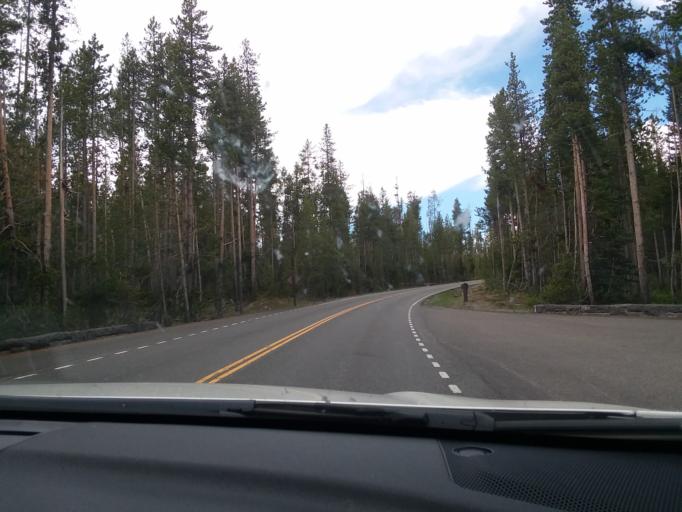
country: US
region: Idaho
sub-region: Teton County
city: Driggs
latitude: 44.1520
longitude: -110.6737
